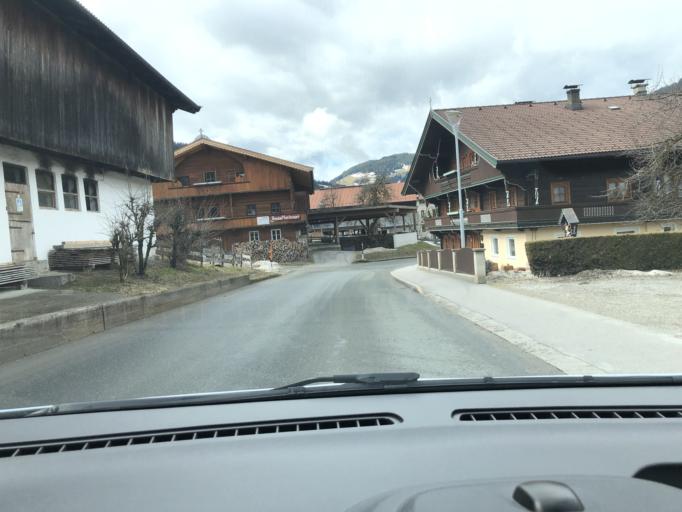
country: AT
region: Tyrol
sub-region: Politischer Bezirk Kitzbuhel
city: Itter
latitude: 47.4480
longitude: 12.0960
